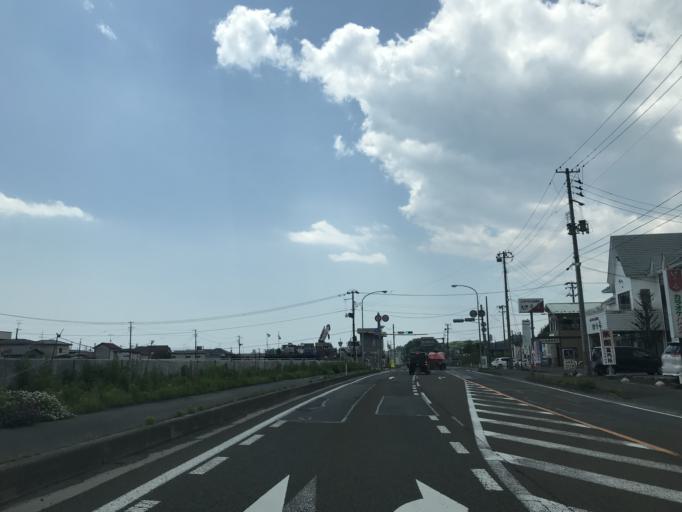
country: JP
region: Miyagi
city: Matsushima
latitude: 38.3866
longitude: 141.0679
